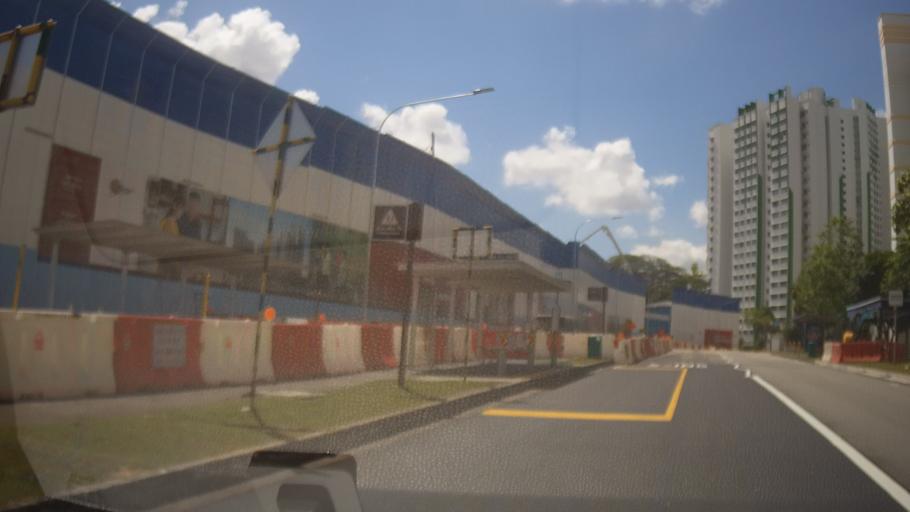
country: MY
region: Johor
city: Johor Bahru
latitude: 1.4364
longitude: 103.7735
